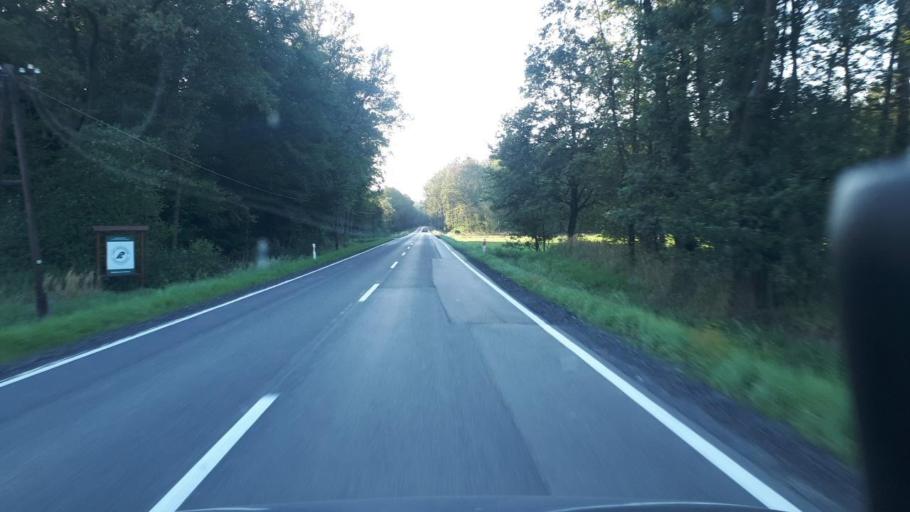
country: PL
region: Opole Voivodeship
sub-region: Powiat oleski
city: Olesno
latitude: 50.8473
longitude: 18.4799
